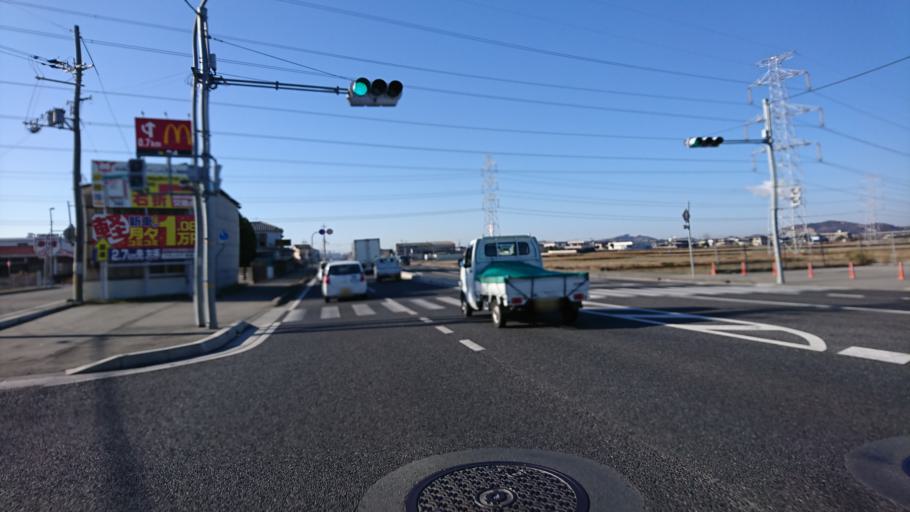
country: JP
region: Hyogo
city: Kakogawacho-honmachi
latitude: 34.7998
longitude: 134.8299
